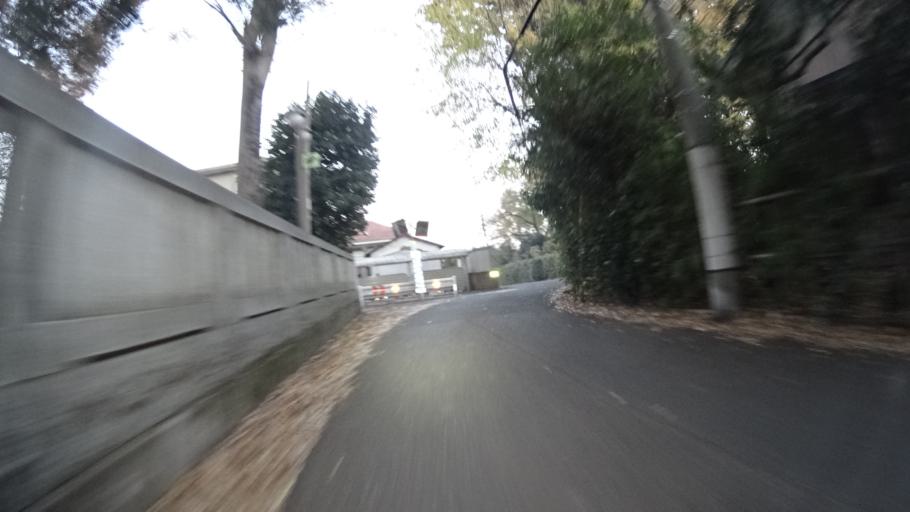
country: JP
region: Tokyo
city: Hino
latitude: 35.6815
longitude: 139.4231
